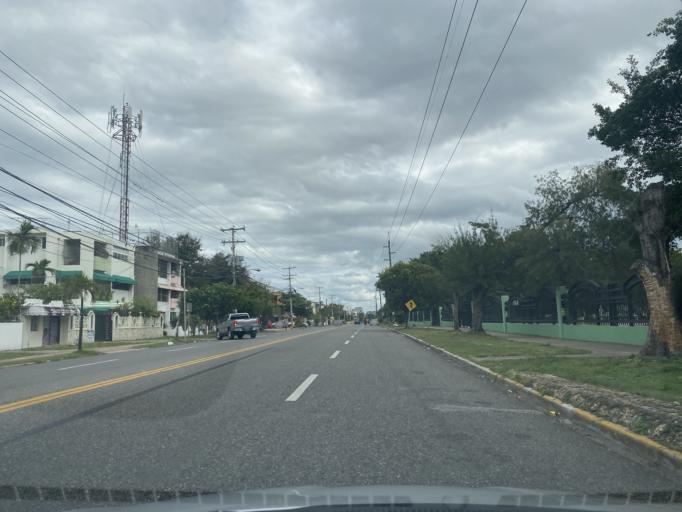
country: DO
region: Santo Domingo
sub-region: Santo Domingo
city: Santo Domingo Este
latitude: 18.4811
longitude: -69.8537
